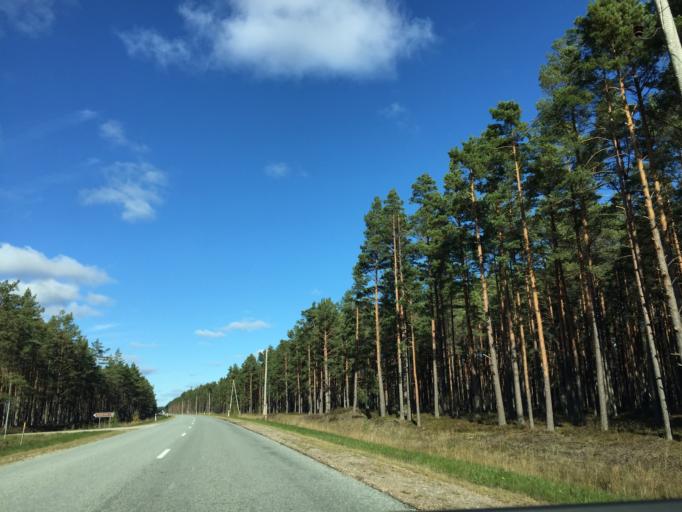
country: LV
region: Mesraga
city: Mersrags
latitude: 57.2610
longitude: 23.1720
